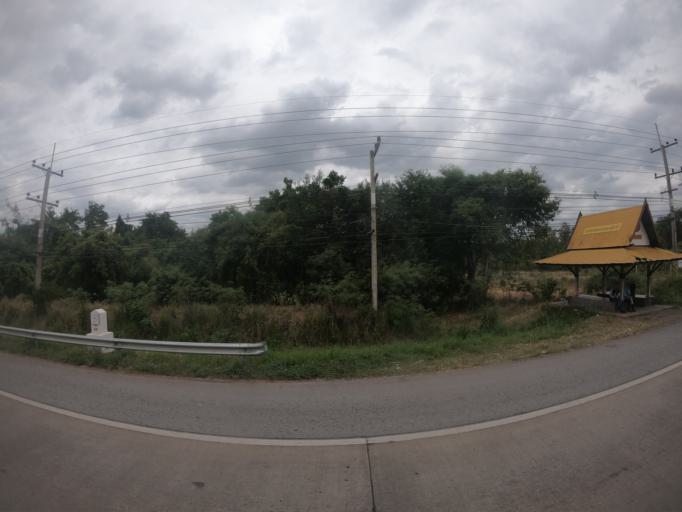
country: TH
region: Nakhon Ratchasima
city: Chok Chai
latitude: 14.7869
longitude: 102.1661
